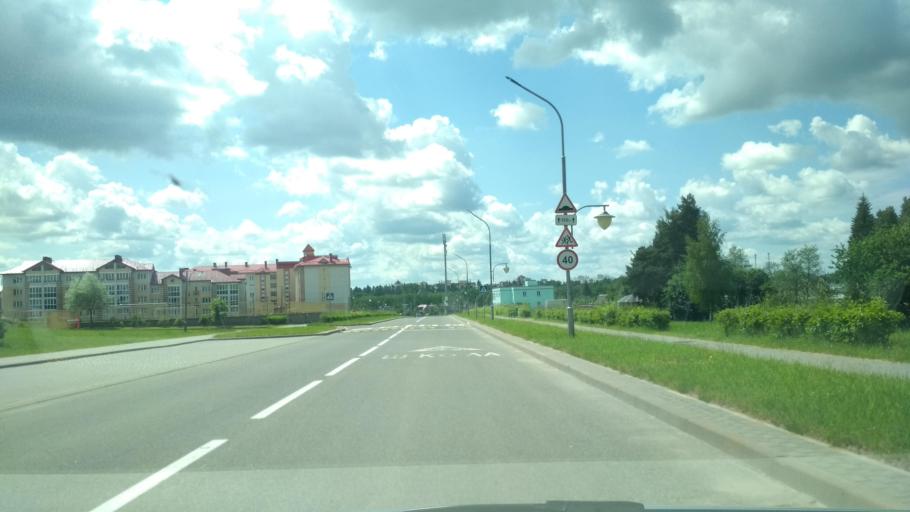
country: BY
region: Grodnenskaya
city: Astravyets
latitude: 54.6175
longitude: 25.9771
